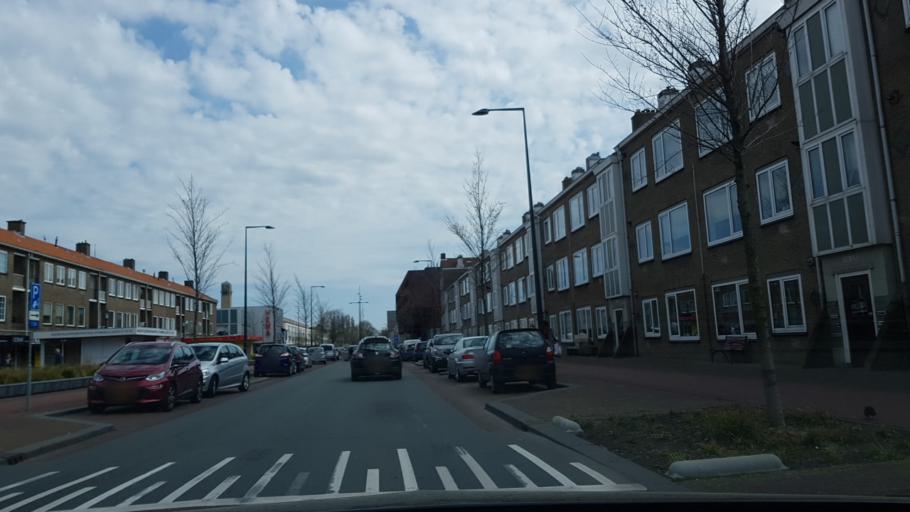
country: NL
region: North Holland
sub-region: Gemeente Velsen
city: Velsen-Zuid
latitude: 52.4586
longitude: 4.6179
